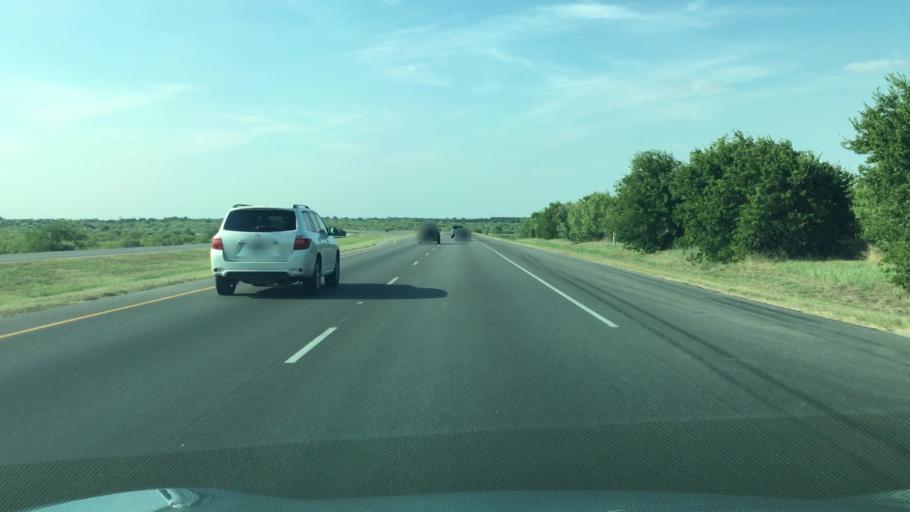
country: US
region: Texas
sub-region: Hays County
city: Kyle
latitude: 30.0320
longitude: -97.8725
